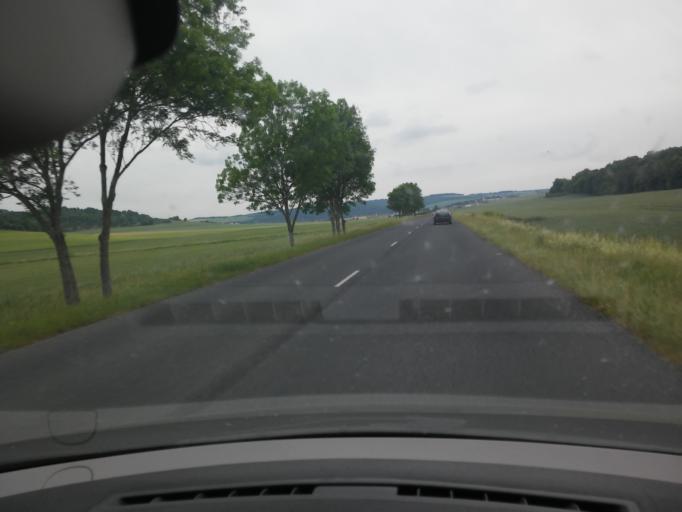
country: FR
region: Lorraine
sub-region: Departement de la Meuse
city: Saint-Mihiel
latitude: 48.9009
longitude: 5.4829
